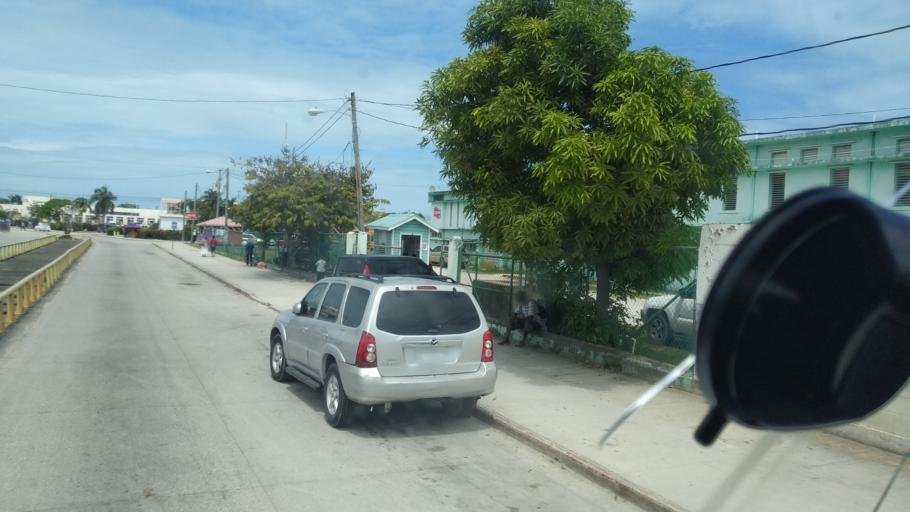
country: BZ
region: Belize
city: Belize City
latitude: 17.5050
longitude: -88.1962
